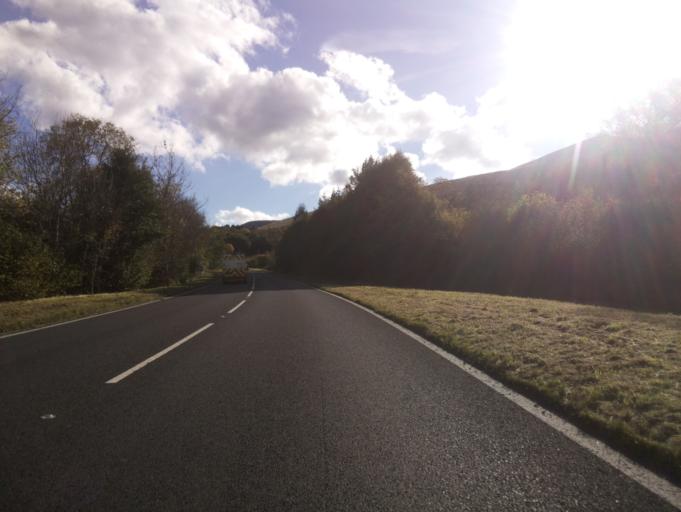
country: GB
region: Wales
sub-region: Sir Powys
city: Brecon
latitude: 51.8910
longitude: -3.4962
